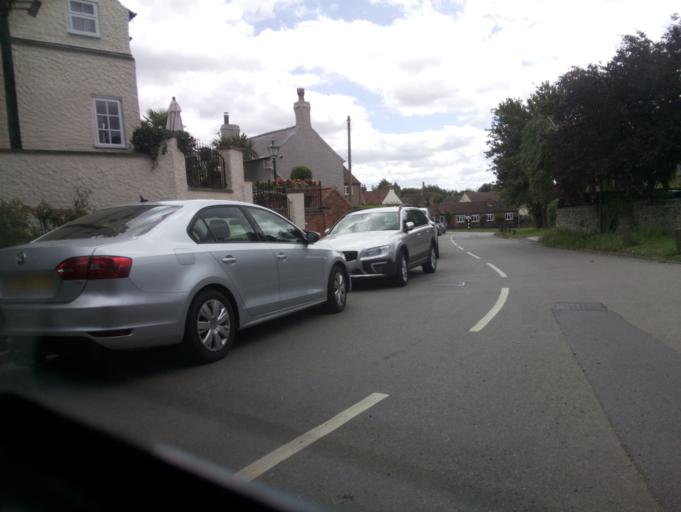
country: GB
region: England
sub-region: Nottinghamshire
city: Ruddington
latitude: 52.8406
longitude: -1.1043
